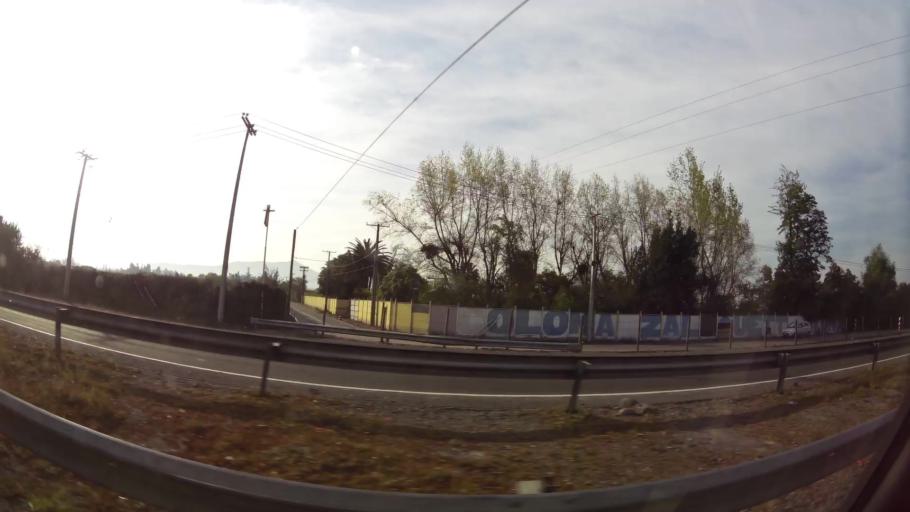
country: CL
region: Santiago Metropolitan
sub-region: Provincia de Talagante
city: Penaflor
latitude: -33.6456
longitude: -70.8775
